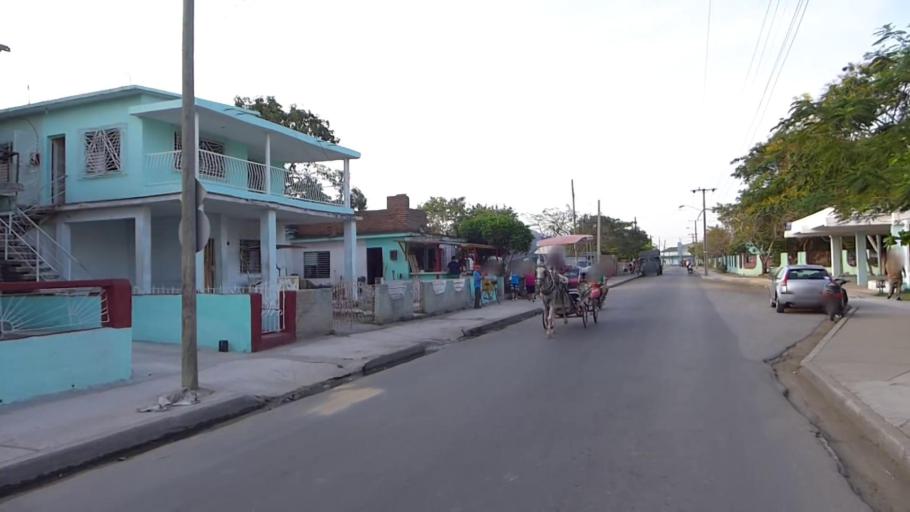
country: CU
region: Camaguey
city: Camaguey
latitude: 21.3831
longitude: -77.9362
